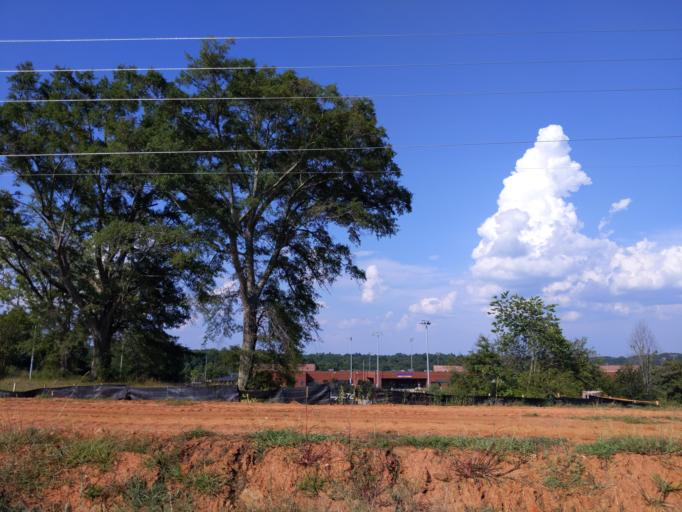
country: US
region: Georgia
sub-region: Hall County
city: Flowery Branch
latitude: 34.1487
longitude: -83.8893
